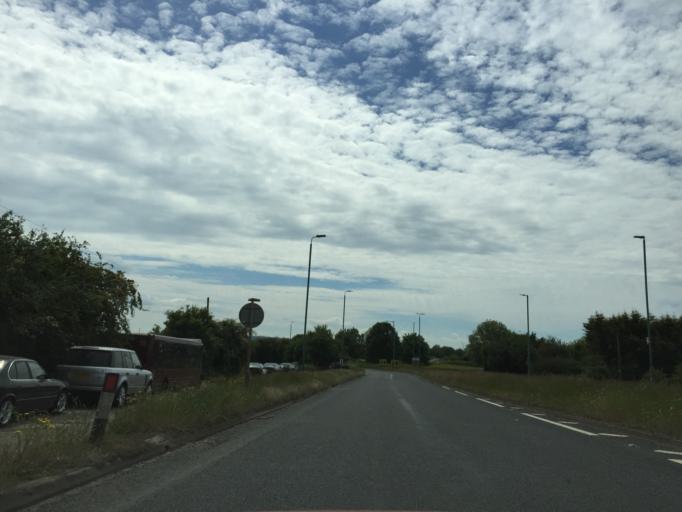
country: GB
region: England
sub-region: Gloucestershire
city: Stonehouse
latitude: 51.7661
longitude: -2.3293
